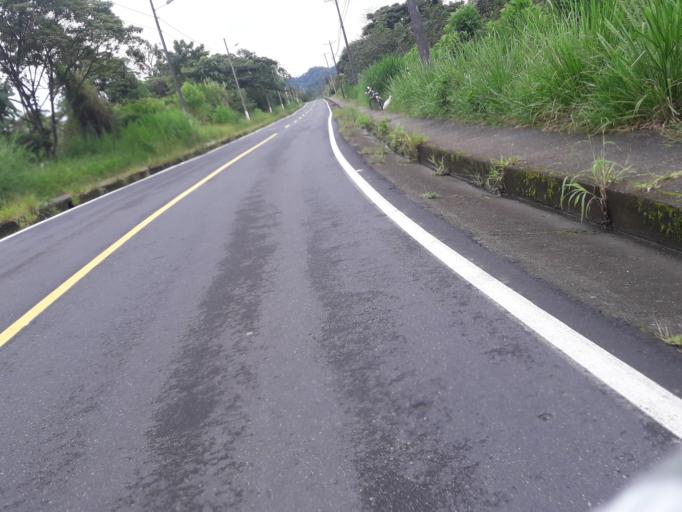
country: EC
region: Napo
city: Tena
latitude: -0.9639
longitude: -77.8567
